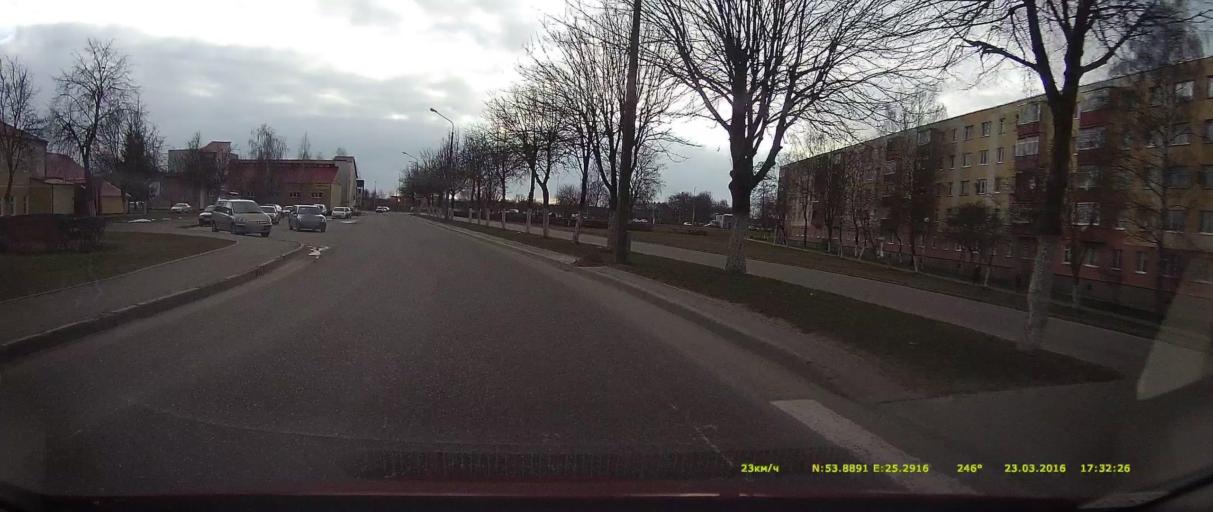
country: BY
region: Grodnenskaya
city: Lida
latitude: 53.8891
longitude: 25.2914
